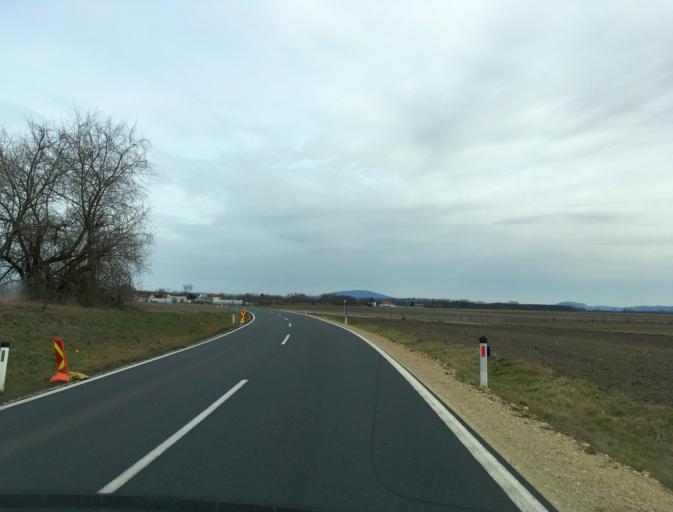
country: AT
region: Lower Austria
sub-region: Politischer Bezirk Ganserndorf
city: Lassee
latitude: 48.2207
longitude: 16.8048
